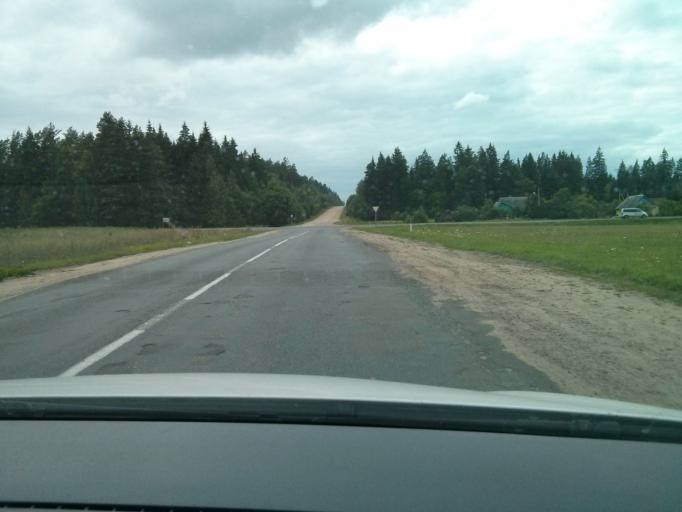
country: BY
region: Minsk
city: Horad Barysaw
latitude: 54.2905
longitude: 28.5295
